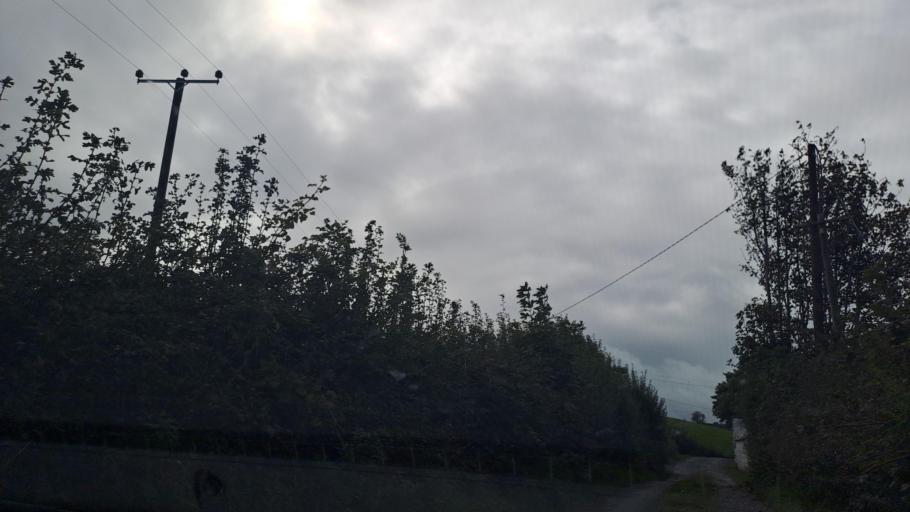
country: IE
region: Ulster
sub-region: An Cabhan
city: Kingscourt
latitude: 53.9751
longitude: -6.8463
